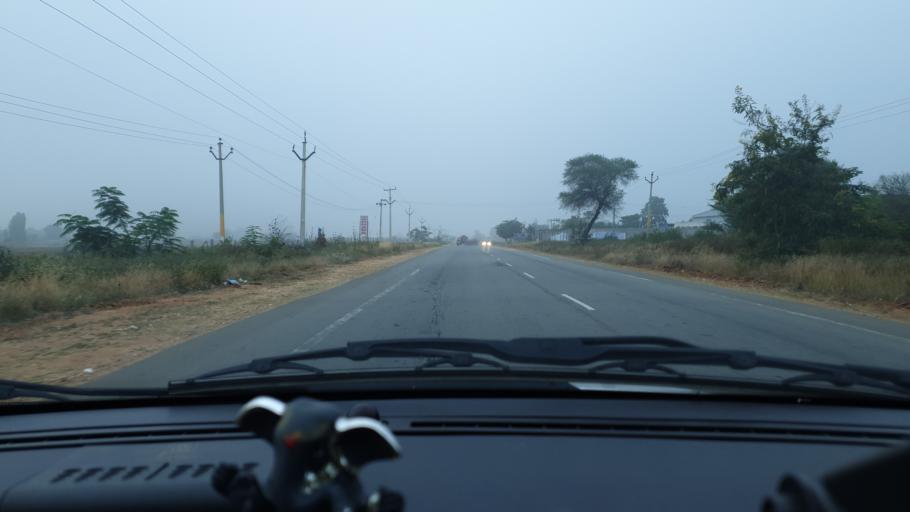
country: IN
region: Telangana
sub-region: Mahbubnagar
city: Farrukhnagar
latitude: 16.9203
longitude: 78.5272
